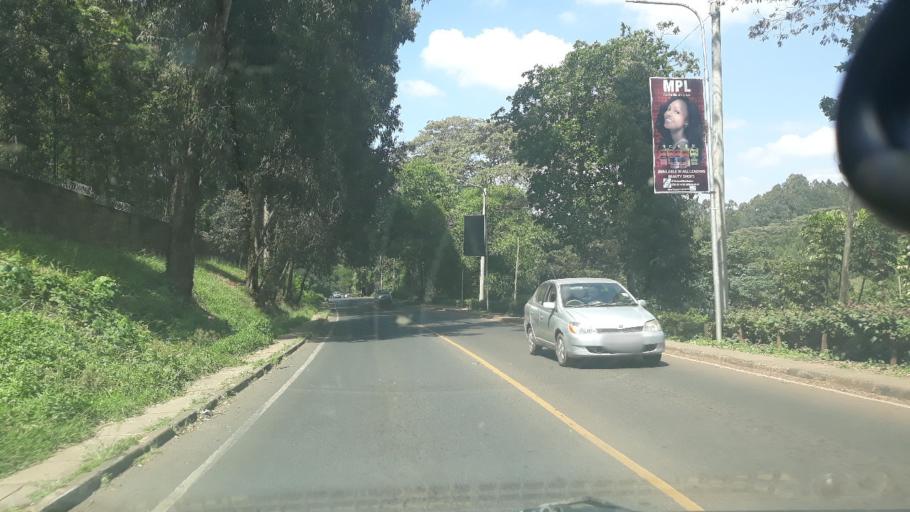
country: KE
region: Nairobi Area
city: Nairobi
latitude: -1.2493
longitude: 36.8202
